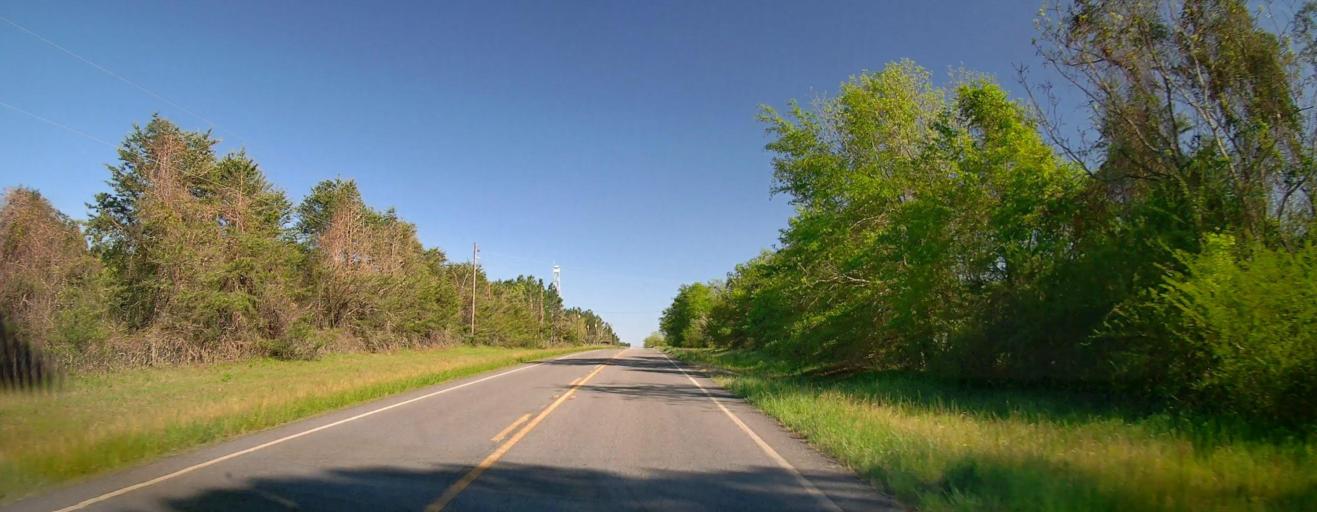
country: US
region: Georgia
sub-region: Wilcox County
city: Rochelle
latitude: 32.0035
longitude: -83.4831
